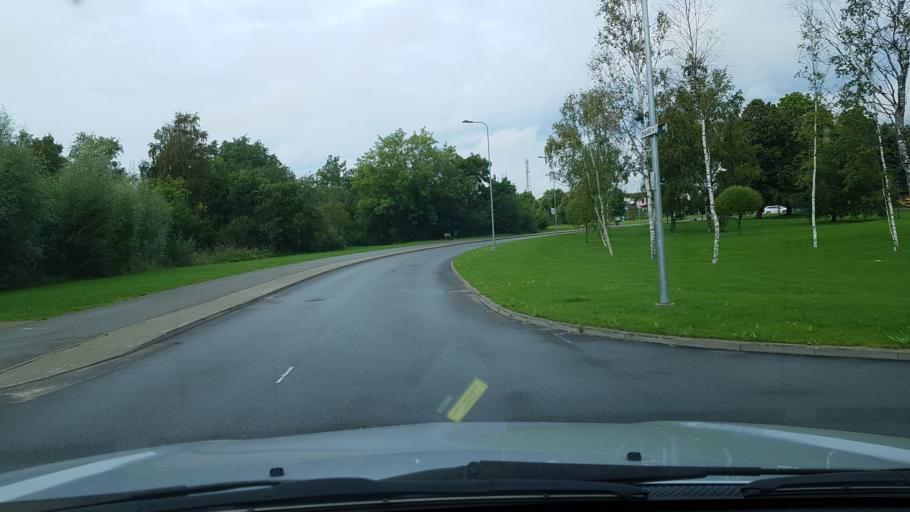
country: EE
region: Harju
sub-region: Rae vald
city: Jueri
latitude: 59.3555
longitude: 24.9148
